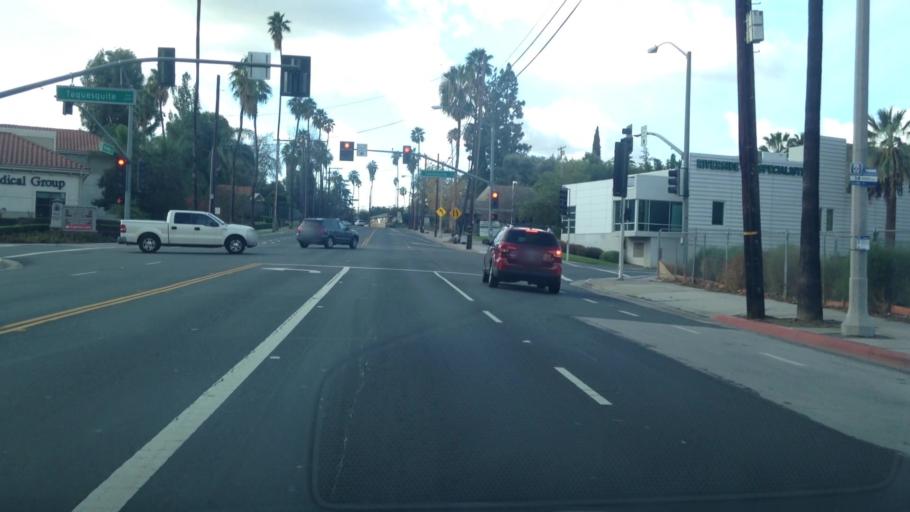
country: US
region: California
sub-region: Riverside County
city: Riverside
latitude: 33.9767
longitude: -117.3853
